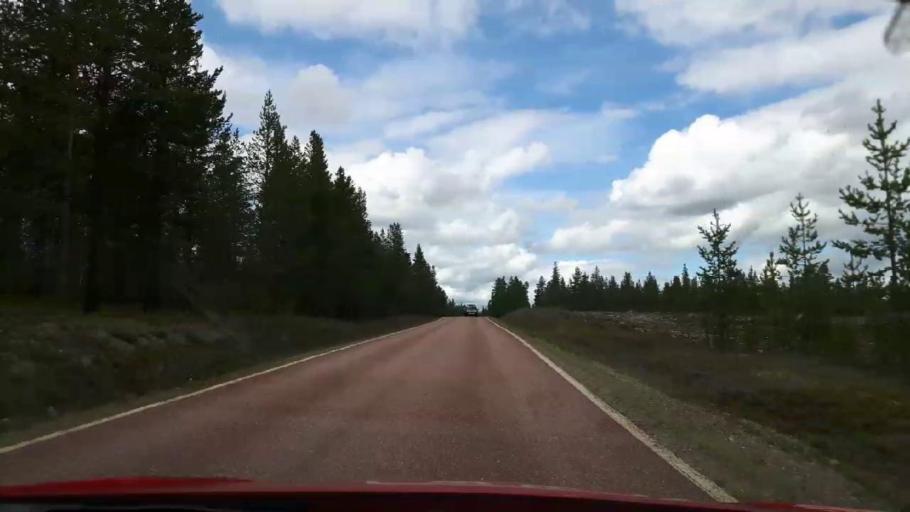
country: NO
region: Hedmark
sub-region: Trysil
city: Innbygda
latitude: 61.8531
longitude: 12.9501
